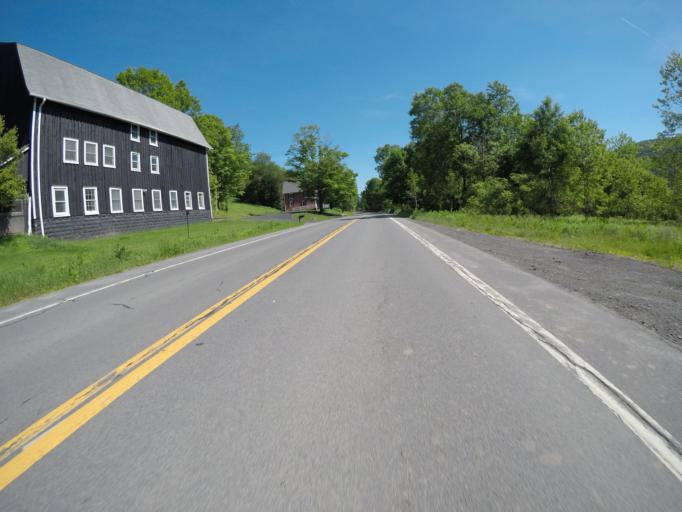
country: US
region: New York
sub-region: Delaware County
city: Delhi
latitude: 42.2333
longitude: -74.9706
